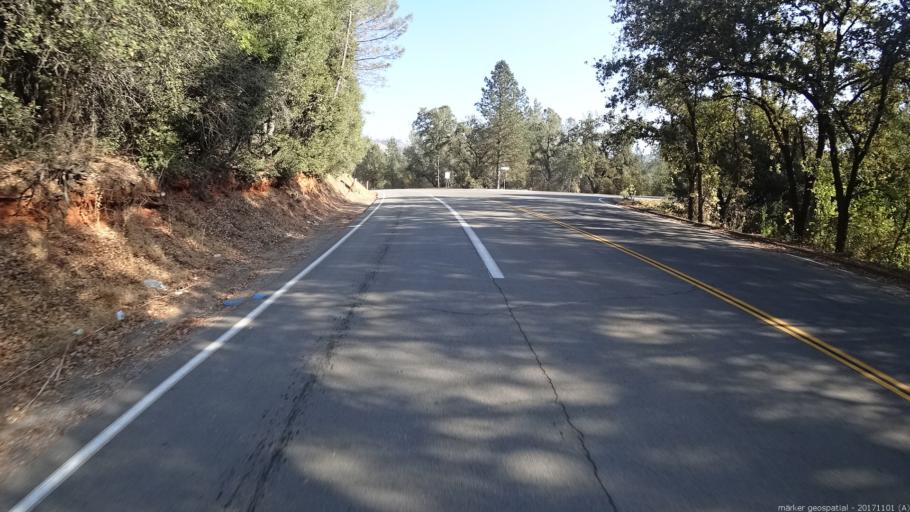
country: US
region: California
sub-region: Shasta County
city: Shasta Lake
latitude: 40.7315
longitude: -122.3234
